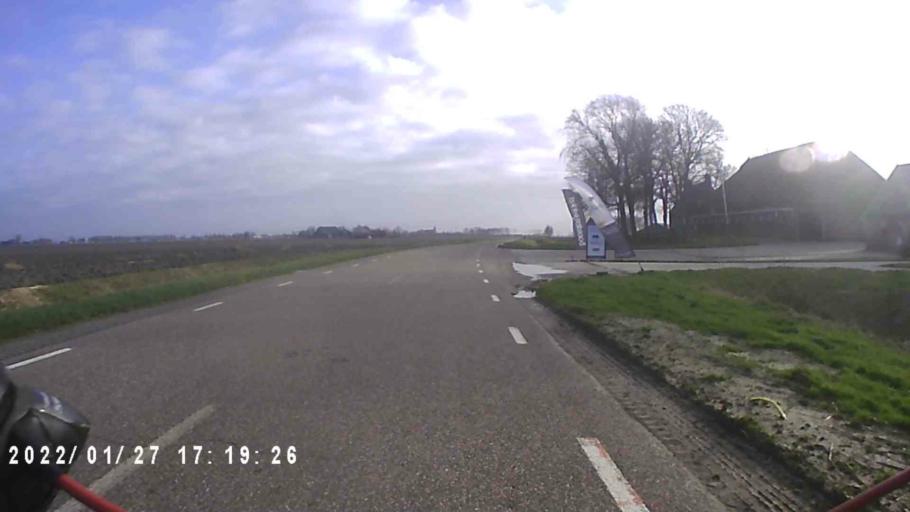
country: NL
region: Friesland
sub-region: Gemeente Dongeradeel
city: Anjum
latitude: 53.3869
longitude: 6.1107
